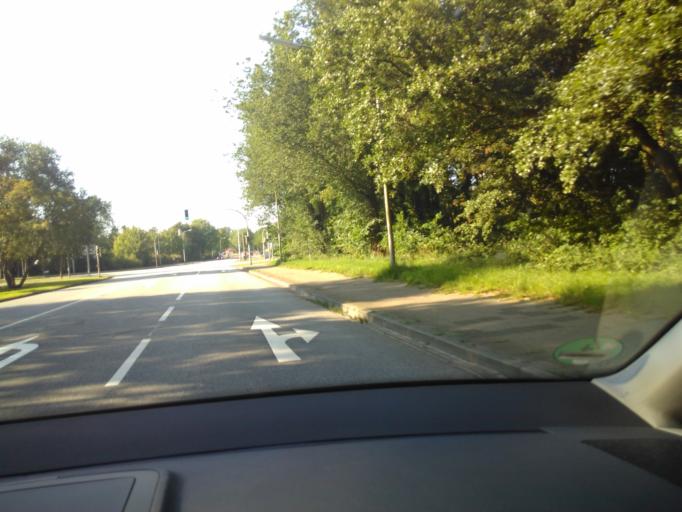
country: DE
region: Lower Saxony
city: Cuxhaven
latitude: 53.8820
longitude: 8.6485
